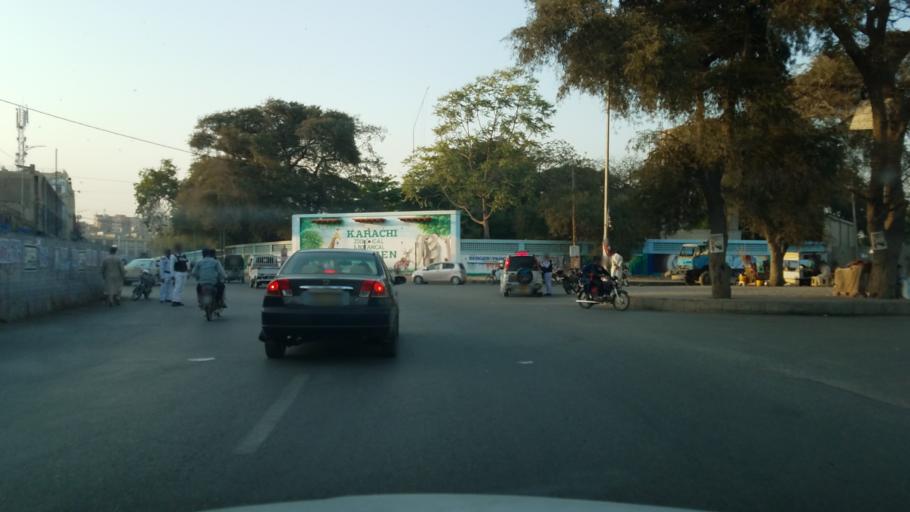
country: PK
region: Sindh
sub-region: Karachi District
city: Karachi
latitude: 24.8735
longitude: 67.0227
